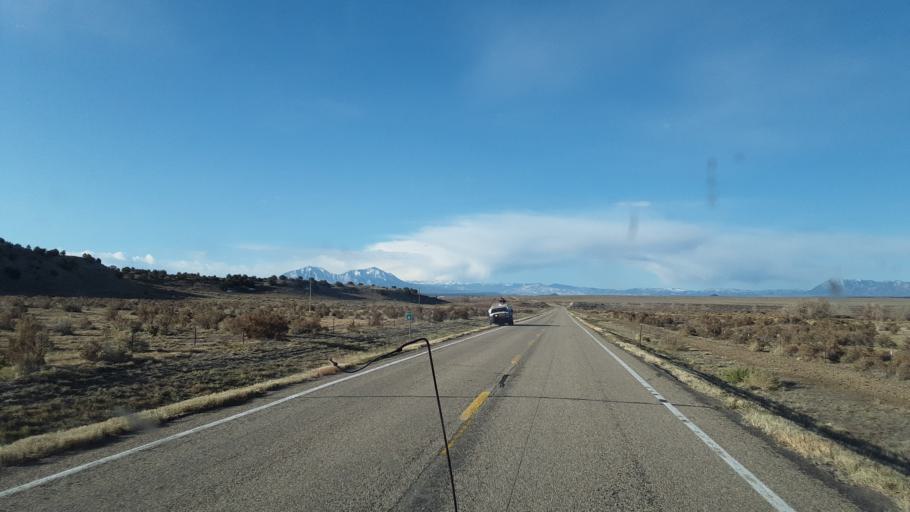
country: US
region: Colorado
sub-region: Huerfano County
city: Walsenburg
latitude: 37.6859
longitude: -104.6435
